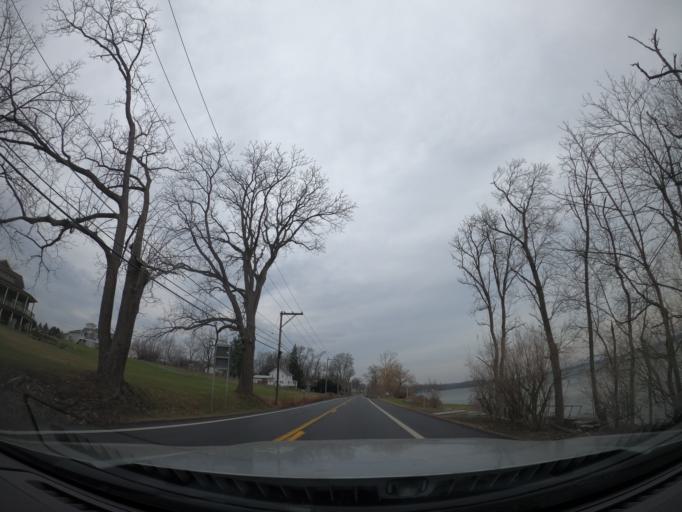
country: US
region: New York
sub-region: Cayuga County
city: Melrose Park
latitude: 42.8730
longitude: -76.5394
